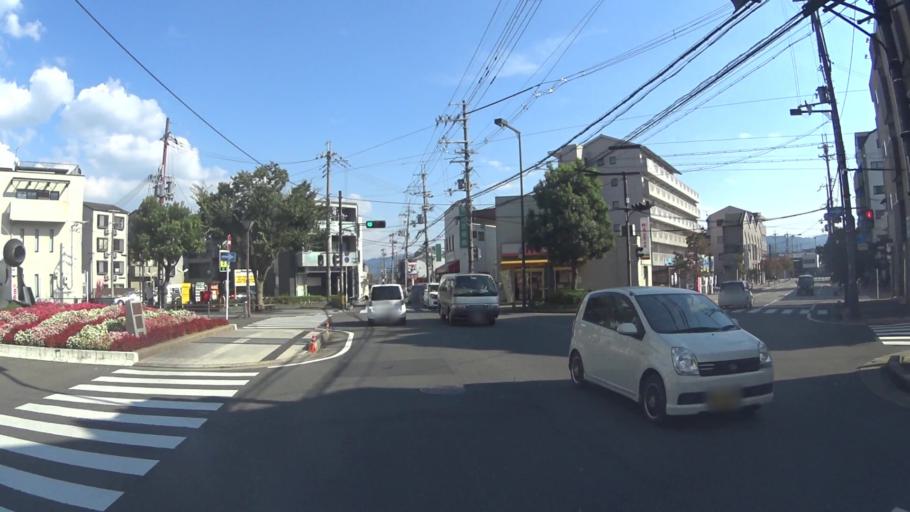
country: JP
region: Kyoto
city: Kameoka
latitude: 35.0324
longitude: 135.5541
